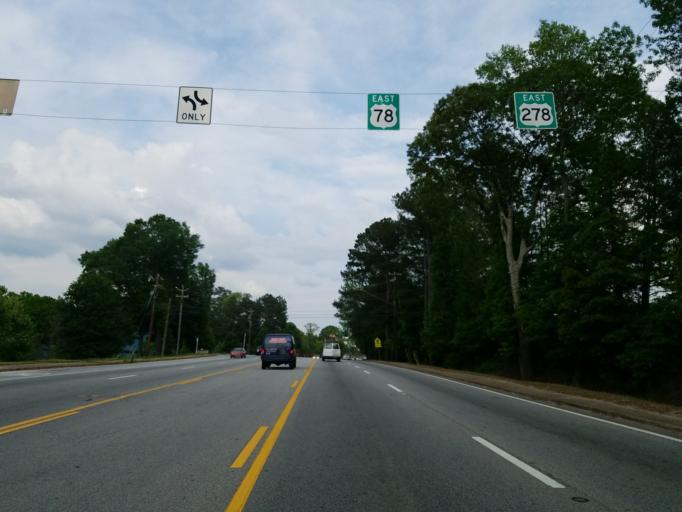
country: US
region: Georgia
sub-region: Cobb County
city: Vinings
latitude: 33.7943
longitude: -84.5040
